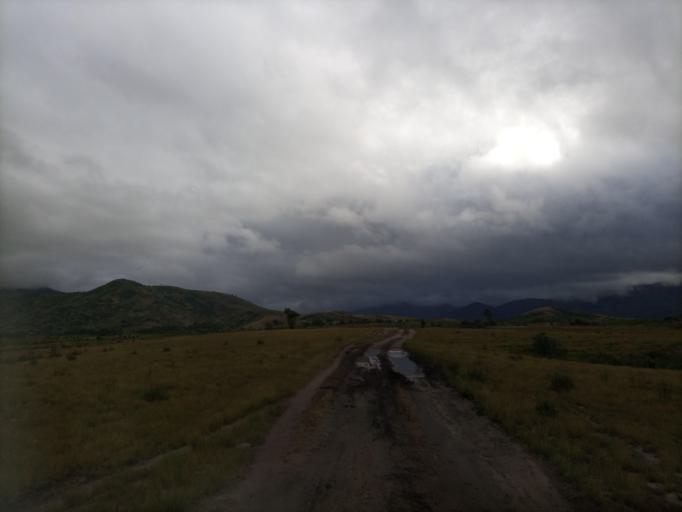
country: MG
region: Anosy
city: Fort Dauphin
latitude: -24.7599
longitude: 47.0751
